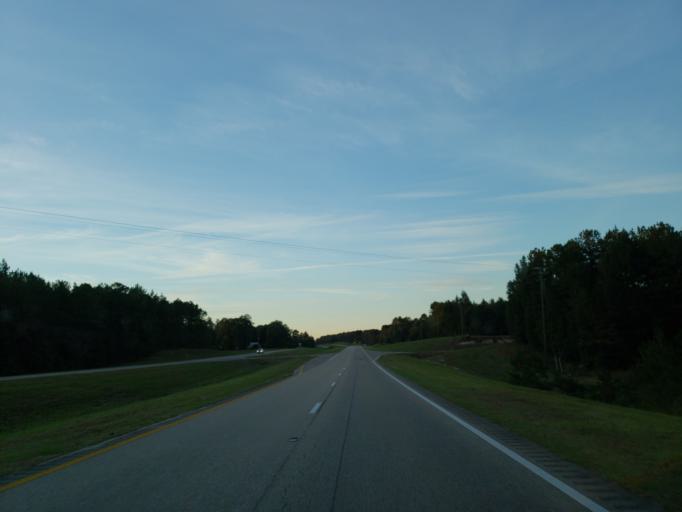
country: US
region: Mississippi
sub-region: Wayne County
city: Belmont
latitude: 31.4922
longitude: -88.4914
